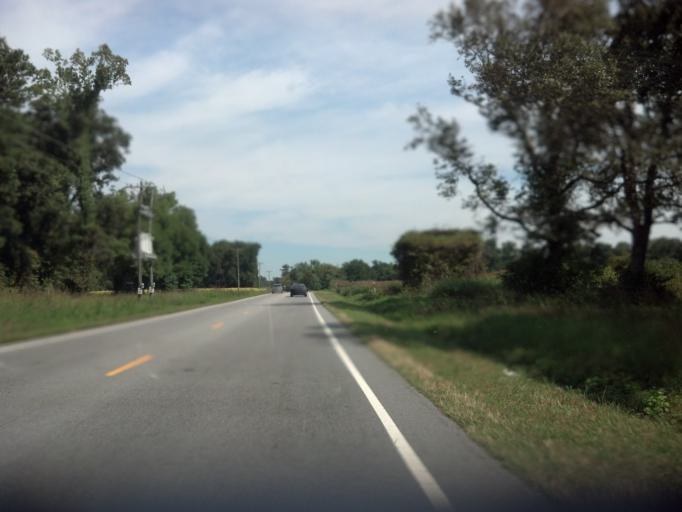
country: US
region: North Carolina
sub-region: Pitt County
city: Farmville
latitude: 35.5623
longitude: -77.6012
